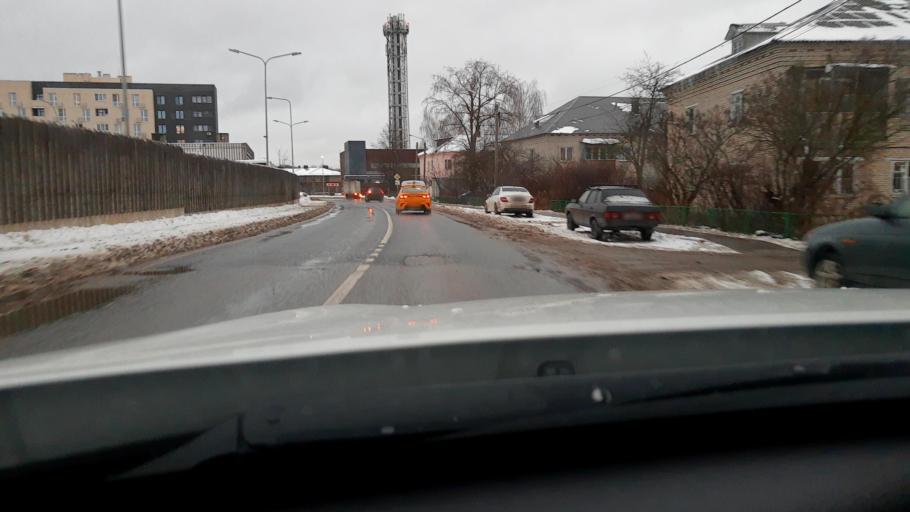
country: RU
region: Moskovskaya
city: Krasnogorsk
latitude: 55.8751
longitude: 37.3126
